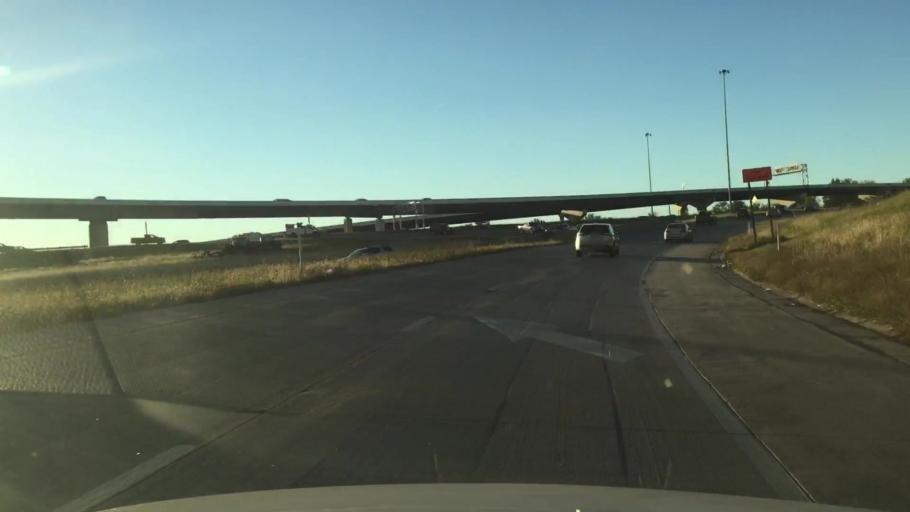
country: US
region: Kansas
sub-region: Johnson County
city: Lenexa
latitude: 38.9360
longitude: -94.7028
